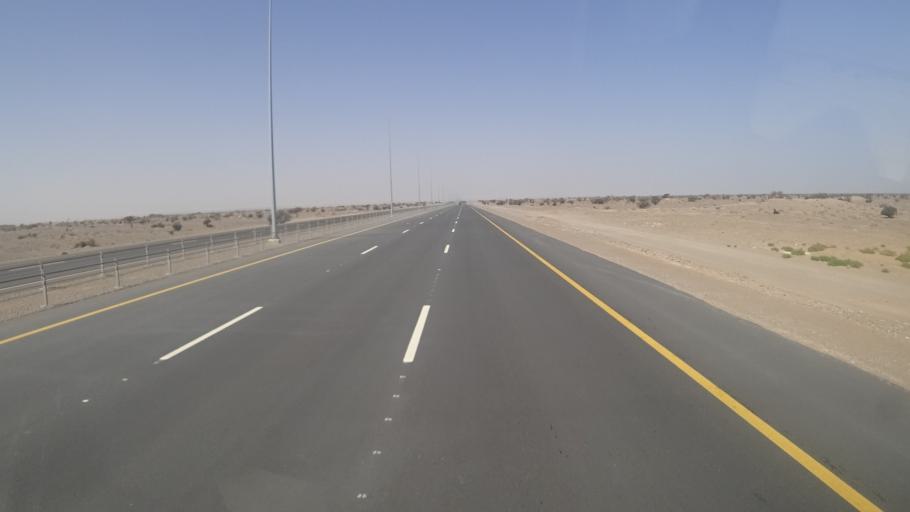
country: OM
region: Ash Sharqiyah
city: Sur
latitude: 22.2748
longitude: 59.2100
